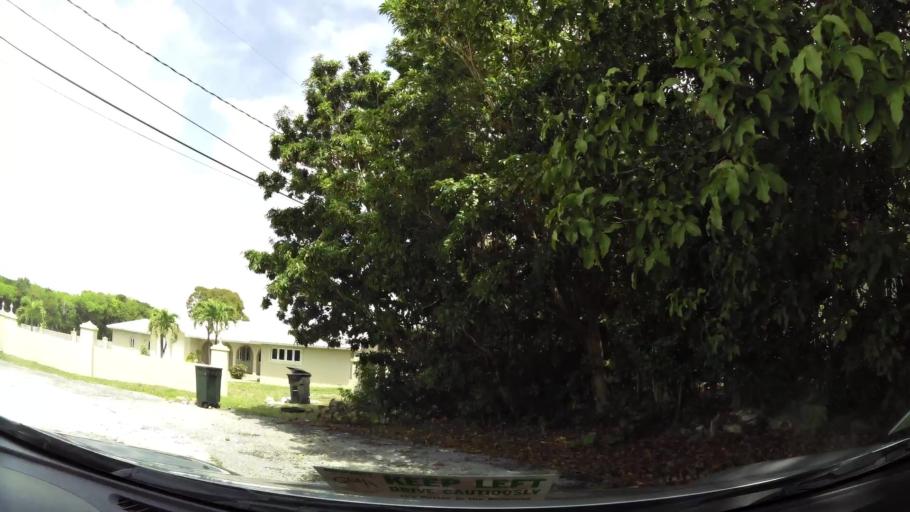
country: BS
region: Freeport
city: Lucaya
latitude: 26.5179
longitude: -78.6498
